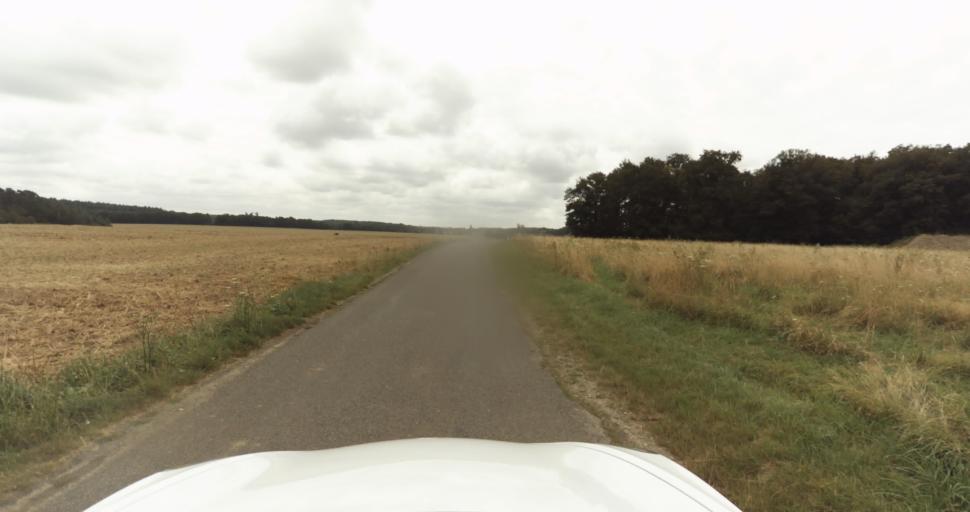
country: FR
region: Haute-Normandie
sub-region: Departement de l'Eure
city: Saint-Sebastien-de-Morsent
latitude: 49.0251
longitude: 1.0620
